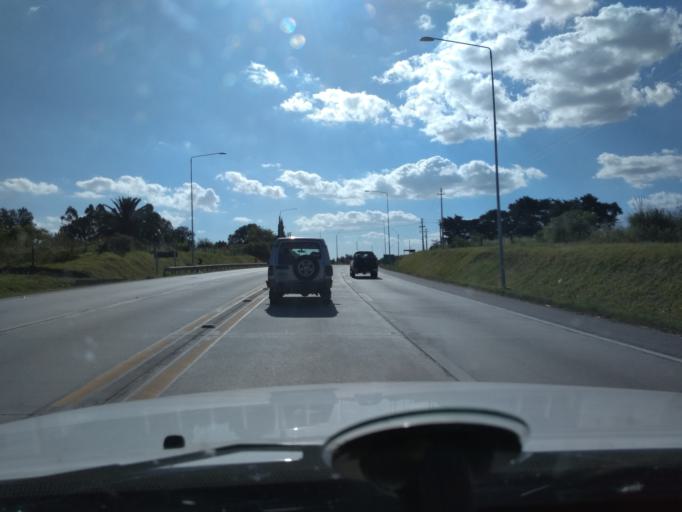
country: UY
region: Canelones
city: La Paz
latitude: -34.7832
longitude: -56.2483
